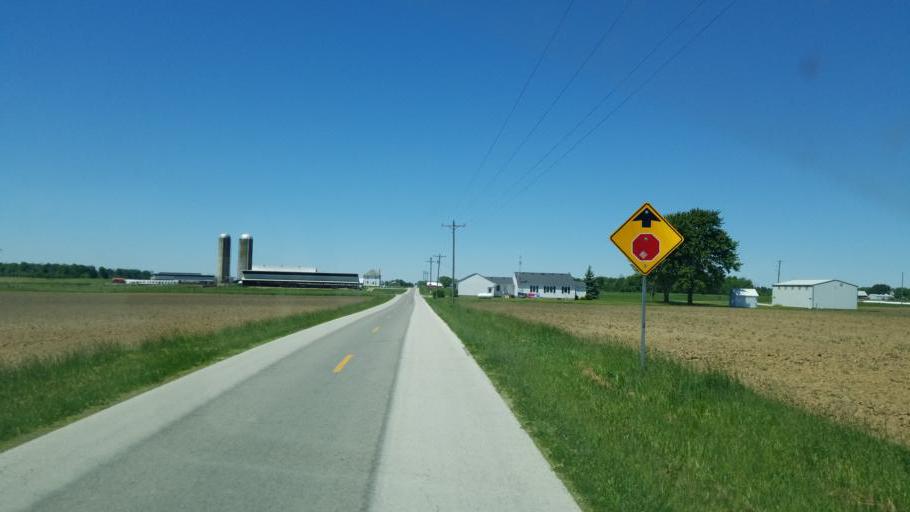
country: US
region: Ohio
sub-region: Auglaize County
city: Minster
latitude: 40.3786
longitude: -84.4630
